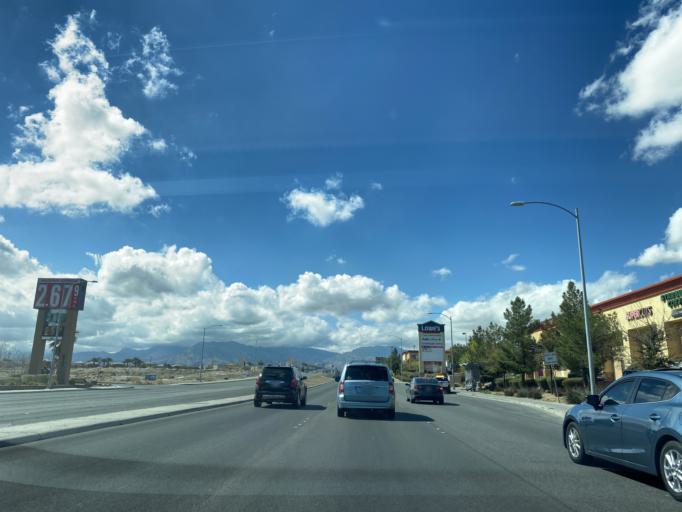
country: US
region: Nevada
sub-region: Clark County
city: Las Vegas
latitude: 36.2391
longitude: -115.2259
